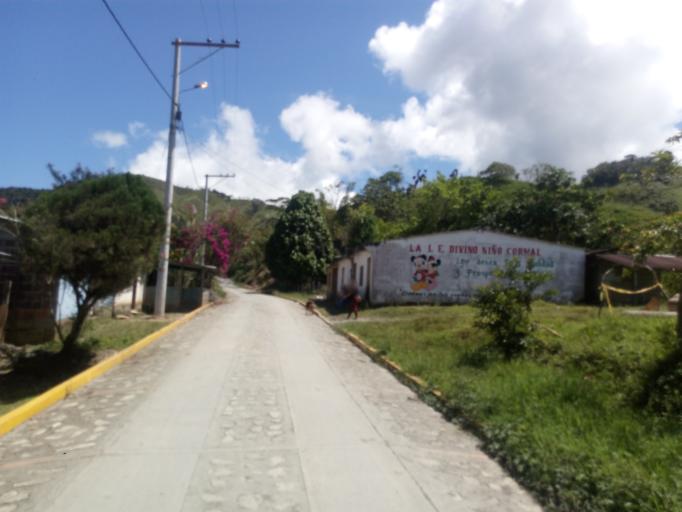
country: CO
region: Boyaca
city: Otanche
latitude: 5.5899
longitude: -74.2259
